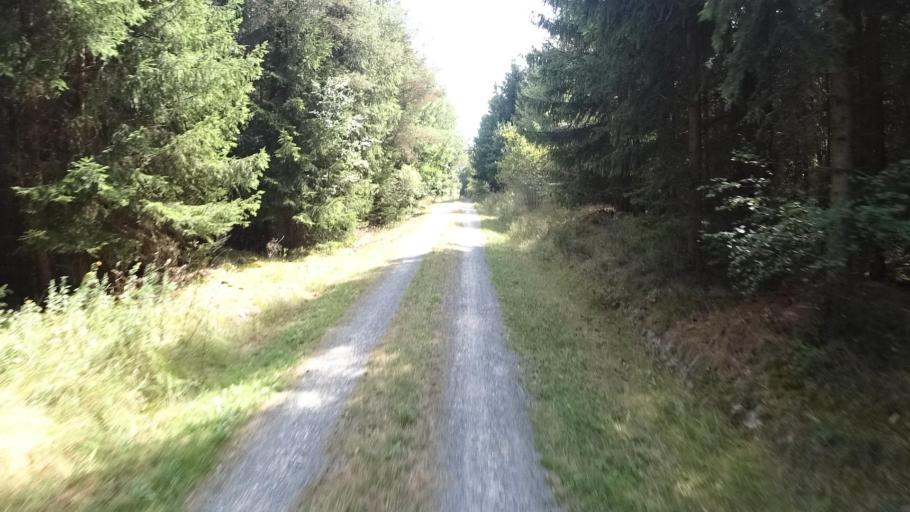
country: DE
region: Rheinland-Pfalz
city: Kisselbach
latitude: 50.0646
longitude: 7.6204
